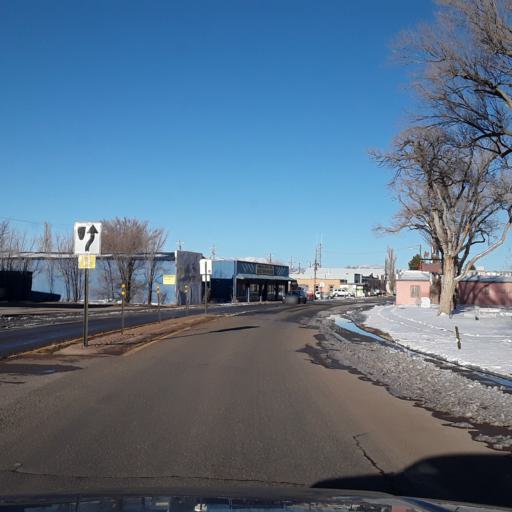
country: US
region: New Mexico
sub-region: Lincoln County
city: Carrizozo
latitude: 33.6417
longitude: -105.8779
